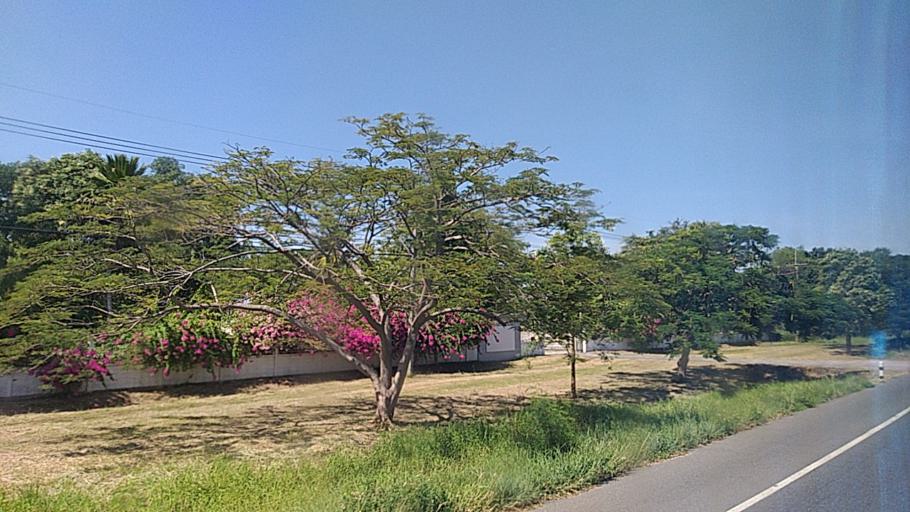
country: TH
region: Khon Kaen
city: Ban Haet
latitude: 16.3034
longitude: 102.7888
